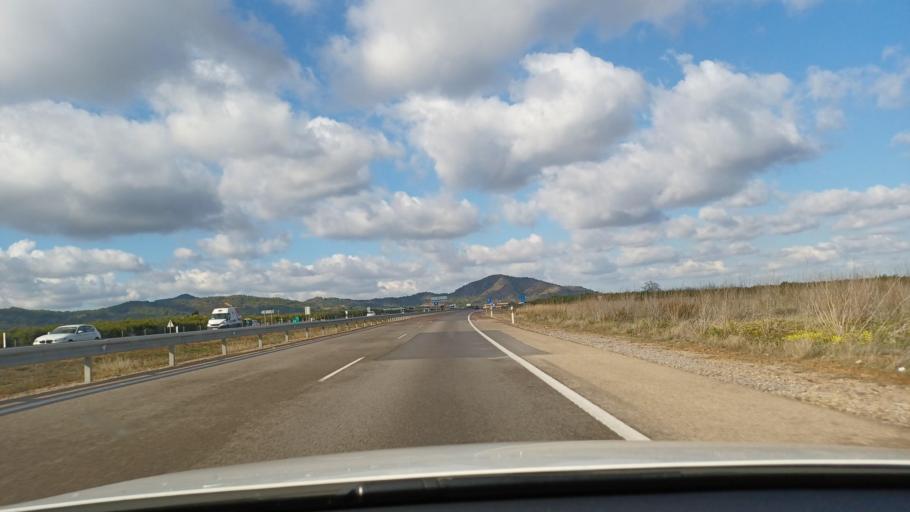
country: ES
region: Valencia
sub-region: Provincia de Castello
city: Villavieja
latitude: 39.8761
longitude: -0.1905
